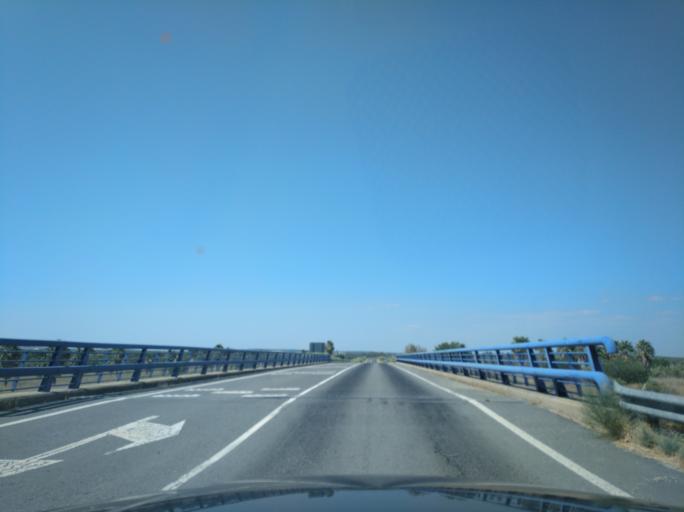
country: ES
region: Andalusia
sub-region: Provincia de Huelva
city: Aljaraque
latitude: 37.3352
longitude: -7.0228
